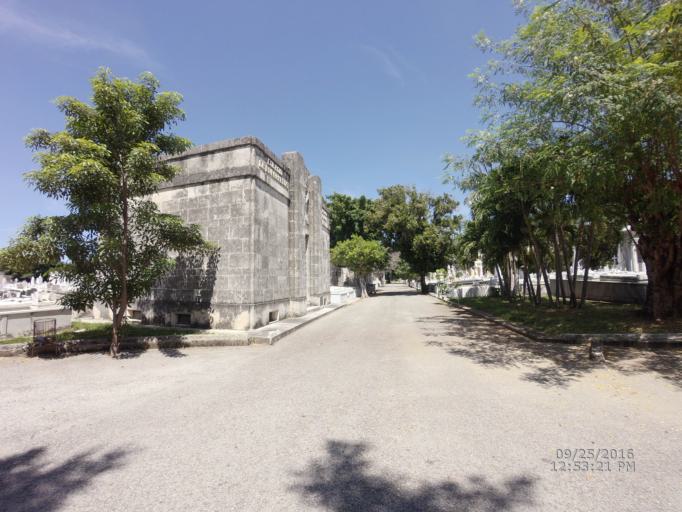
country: CU
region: La Habana
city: Havana
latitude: 23.1217
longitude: -82.3994
